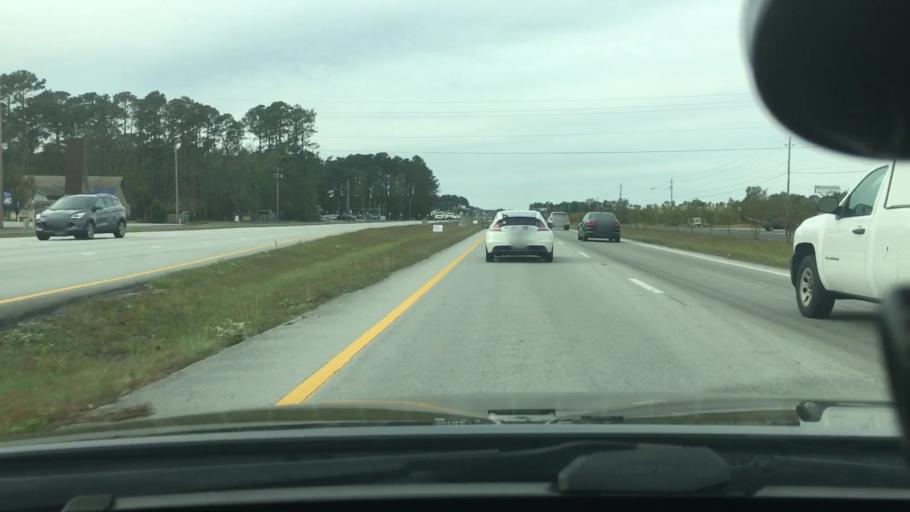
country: US
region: North Carolina
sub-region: Craven County
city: Havelock
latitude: 34.9029
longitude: -76.9319
